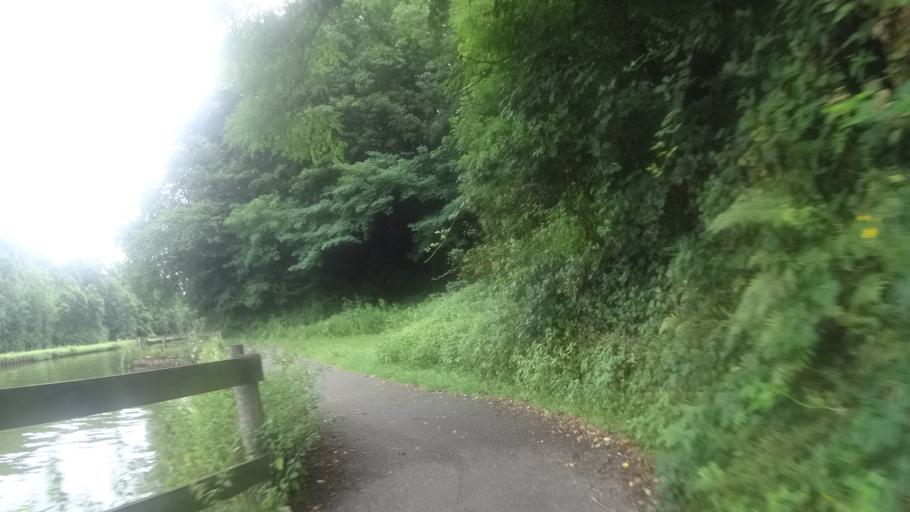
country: FR
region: Alsace
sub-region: Departement du Bas-Rhin
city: Saverne
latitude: 48.7339
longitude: 7.3420
